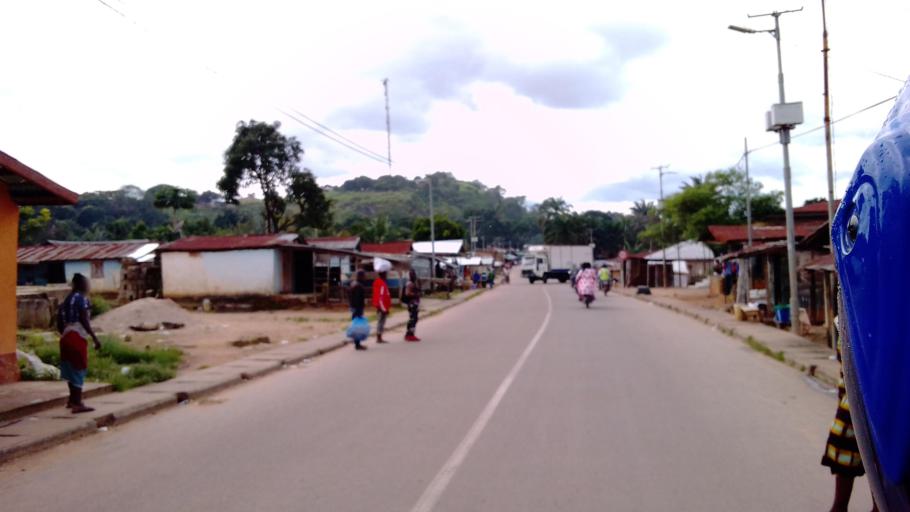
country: SL
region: Eastern Province
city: Koidu
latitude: 8.6473
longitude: -10.9745
